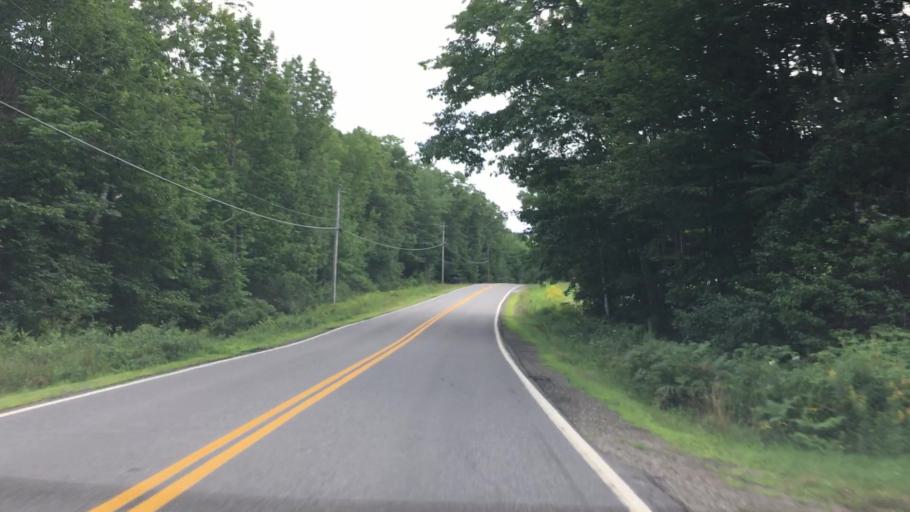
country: US
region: Maine
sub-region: Waldo County
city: Lincolnville
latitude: 44.3366
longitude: -69.0562
